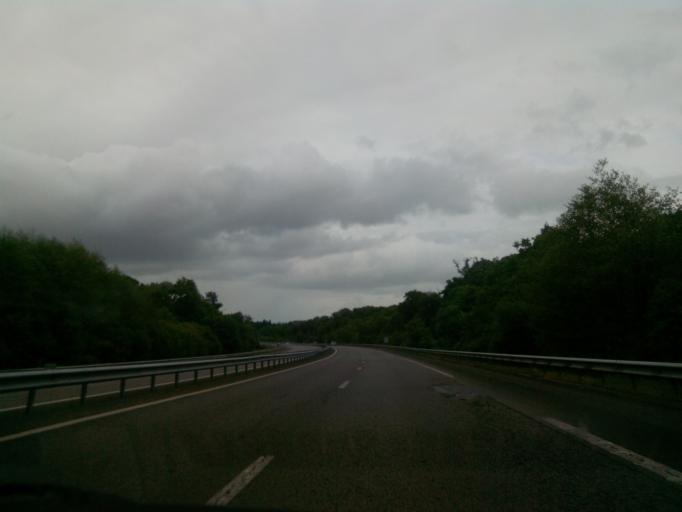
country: FR
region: Brittany
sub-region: Departement du Morbihan
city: Guer
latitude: 47.9459
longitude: -2.0992
